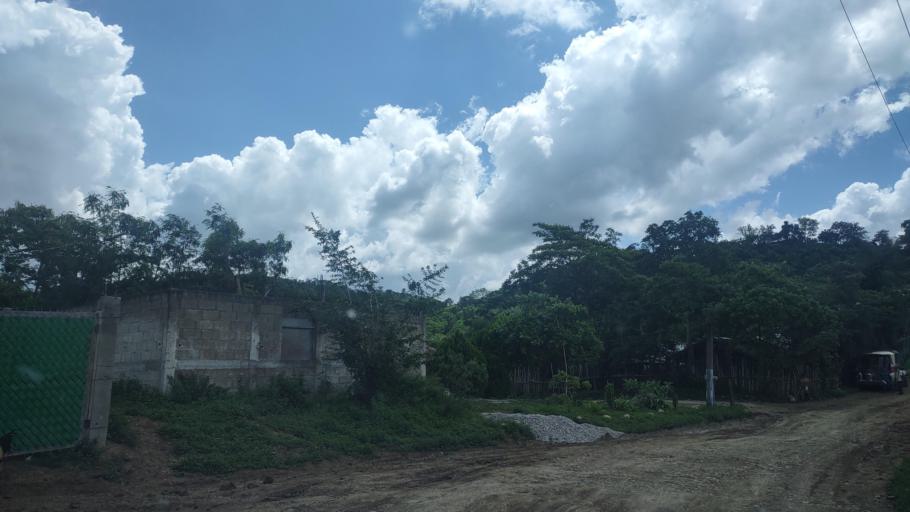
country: MX
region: Veracruz
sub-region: Tantoyuca
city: El Lindero
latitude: 21.3023
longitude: -98.1322
